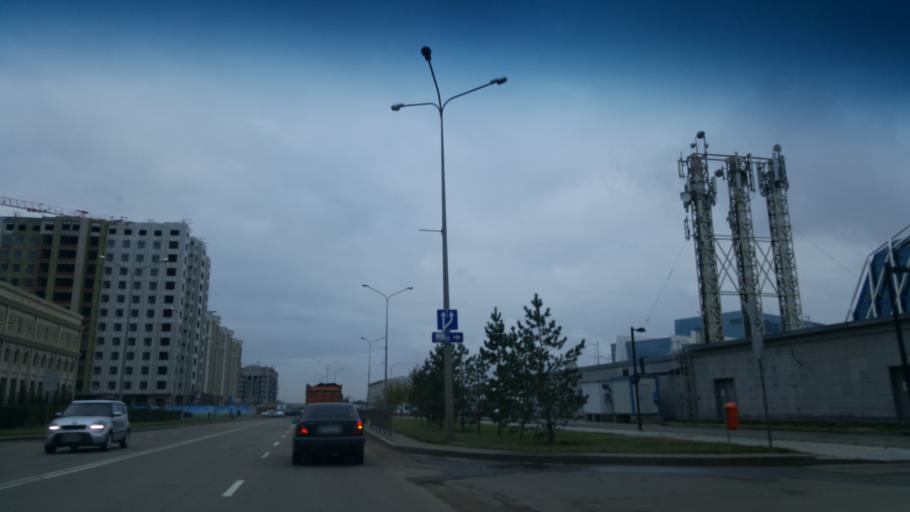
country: KZ
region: Astana Qalasy
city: Astana
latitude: 51.1205
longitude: 71.4738
